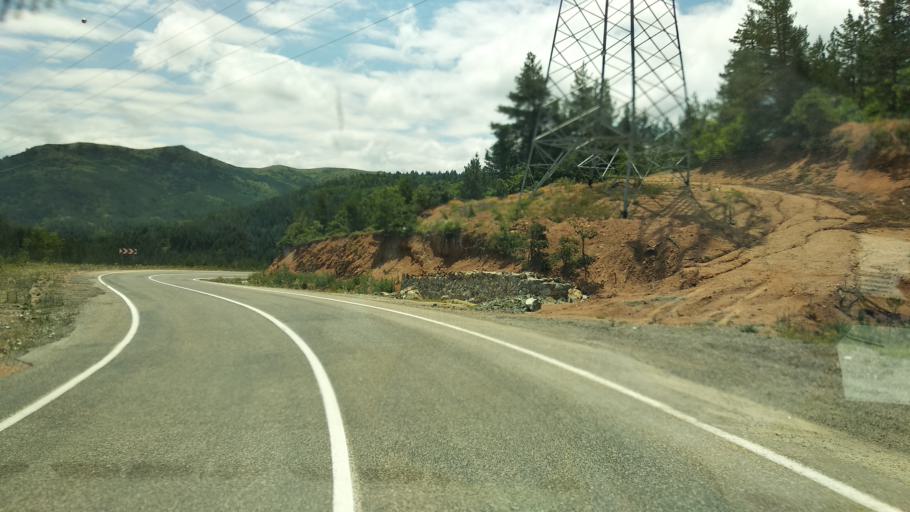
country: TR
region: Gumushane
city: Kose
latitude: 40.2974
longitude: 39.5729
